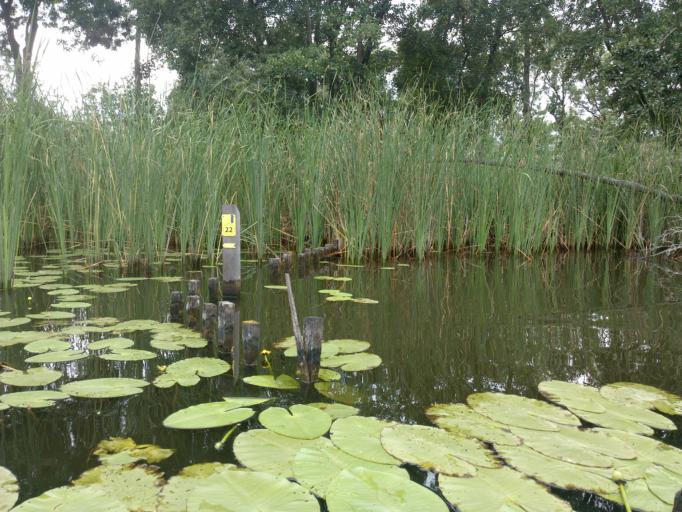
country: NL
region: North Holland
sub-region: Gemeente Wijdemeren
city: Oud-Loosdrecht
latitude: 52.2299
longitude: 5.0753
